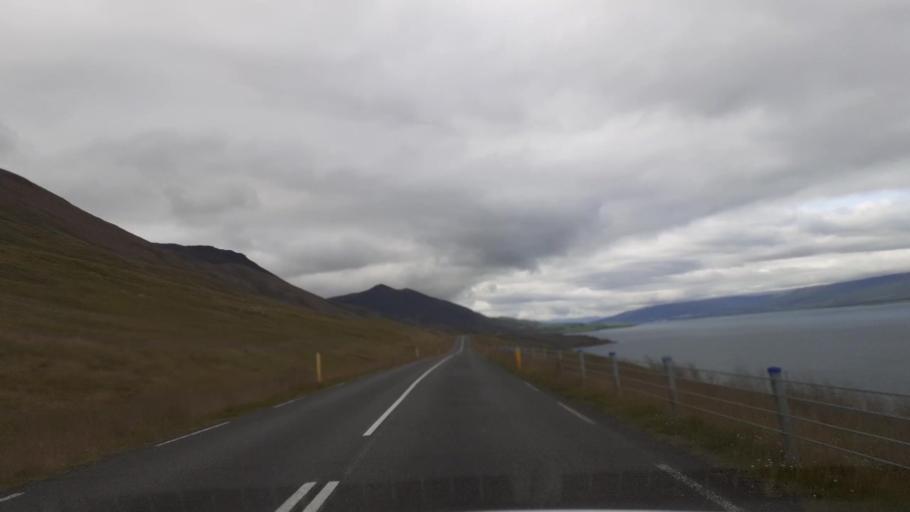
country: IS
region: Northeast
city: Akureyri
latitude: 65.8560
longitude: -18.0619
